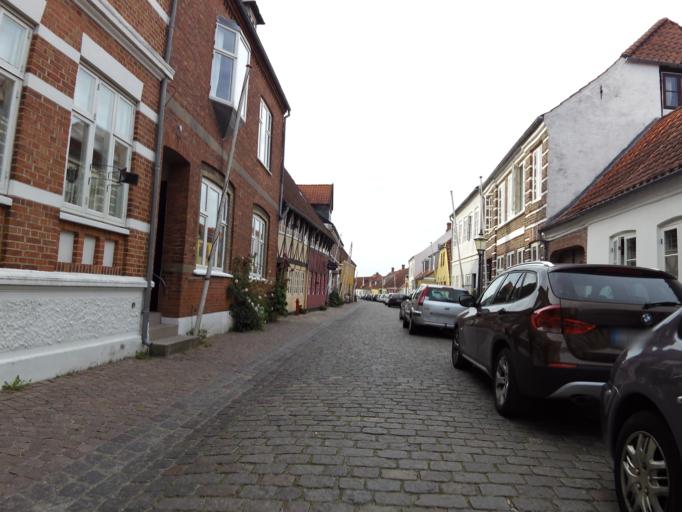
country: DK
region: South Denmark
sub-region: Esbjerg Kommune
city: Ribe
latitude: 55.3292
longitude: 8.7611
